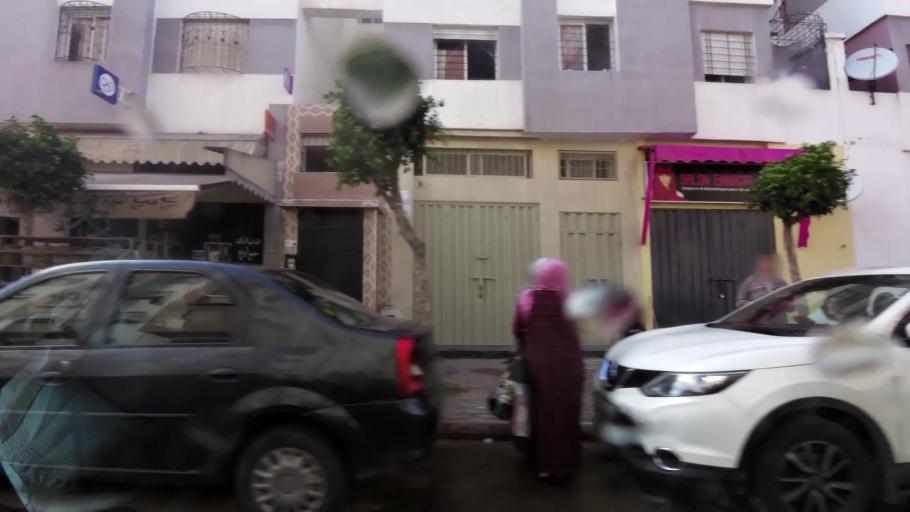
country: MA
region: Grand Casablanca
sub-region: Casablanca
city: Casablanca
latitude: 33.5556
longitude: -7.6992
